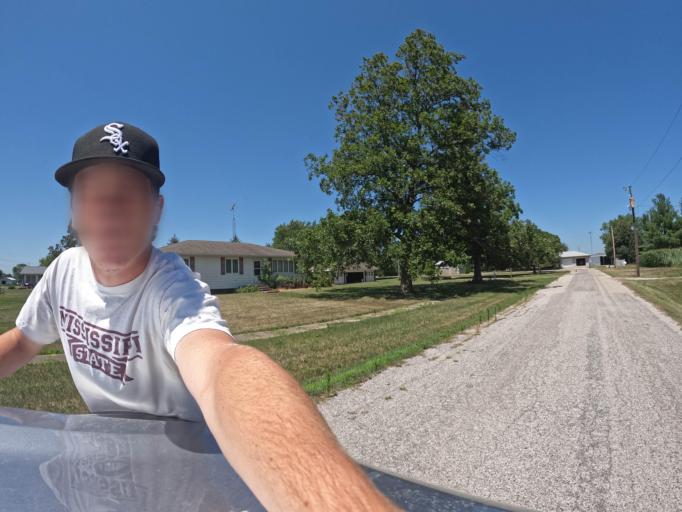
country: US
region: Iowa
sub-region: Keokuk County
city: Sigourney
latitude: 41.4564
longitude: -92.3322
